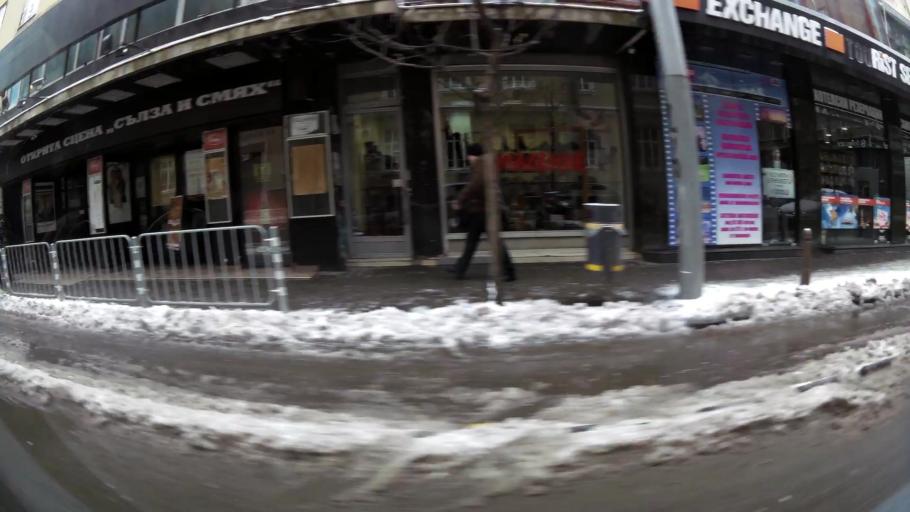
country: BG
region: Sofia-Capital
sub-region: Stolichna Obshtina
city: Sofia
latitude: 42.6938
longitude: 23.3283
